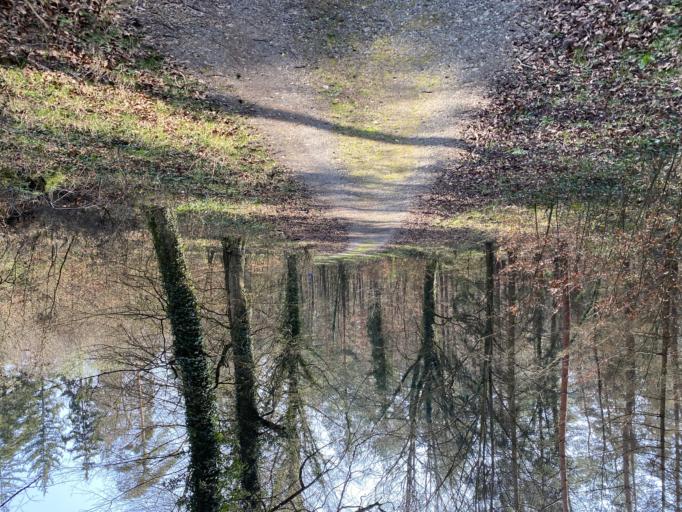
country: DE
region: Baden-Wuerttemberg
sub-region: Karlsruhe Region
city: Eggenstein-Leopoldshafen
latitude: 49.0567
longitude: 8.4120
